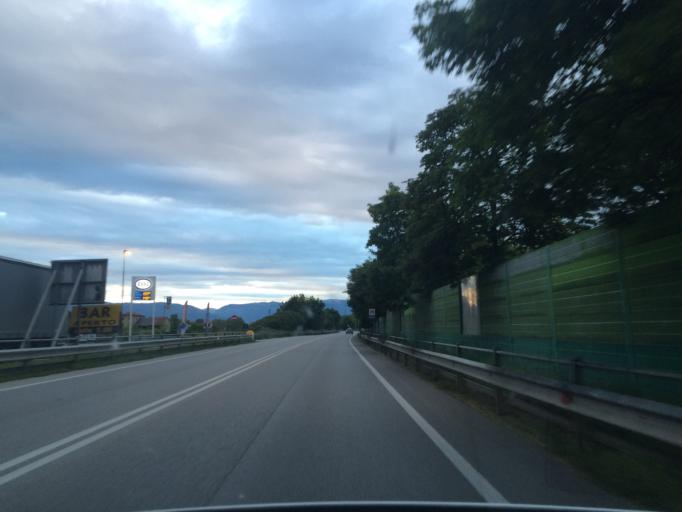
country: IT
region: Veneto
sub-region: Provincia di Padova
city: Cittadella
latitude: 45.6411
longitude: 11.7743
